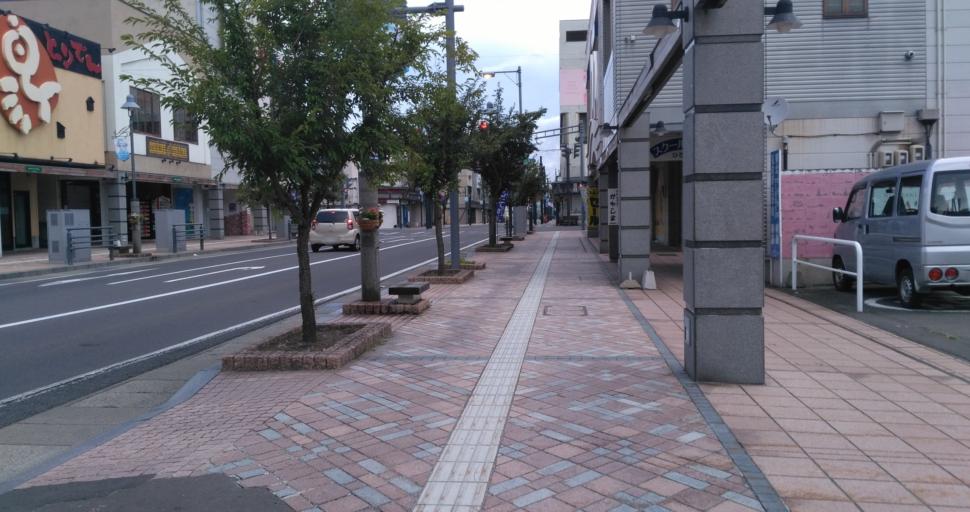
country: JP
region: Aomori
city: Hirosaki
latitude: 40.5980
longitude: 140.4763
